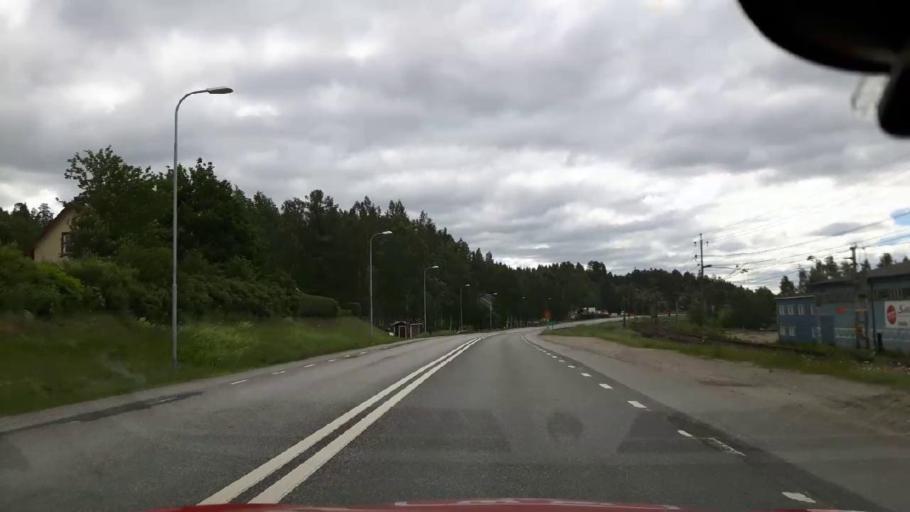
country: SE
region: Jaemtland
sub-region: Braecke Kommun
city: Braecke
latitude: 62.7453
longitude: 15.4237
